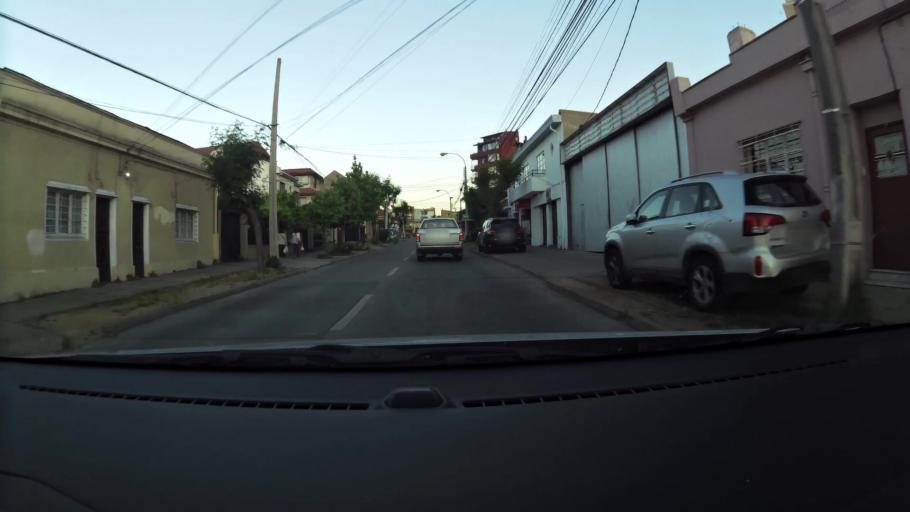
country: CL
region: Valparaiso
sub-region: Provincia de Valparaiso
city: Vina del Mar
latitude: -33.0267
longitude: -71.5709
